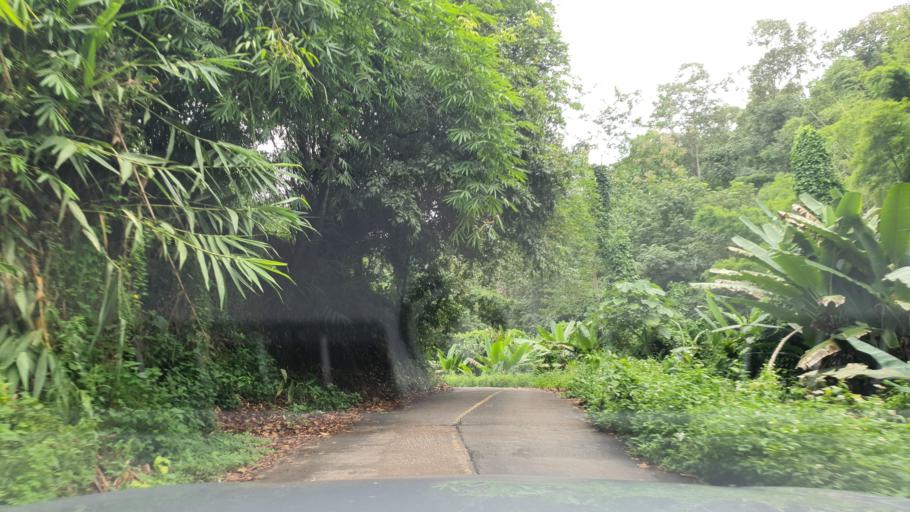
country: TH
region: Chiang Mai
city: Mae Taeng
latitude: 19.2227
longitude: 98.9244
